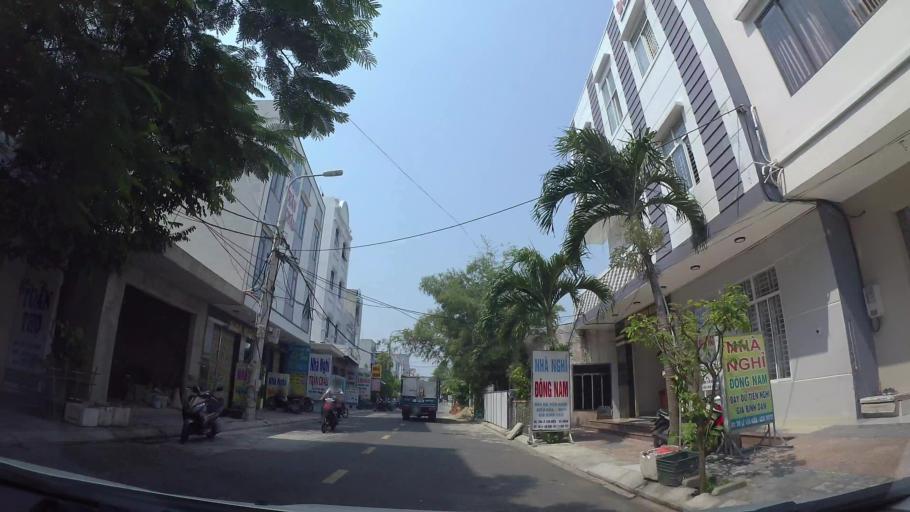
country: VN
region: Da Nang
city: Ngu Hanh Son
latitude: 16.0245
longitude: 108.2495
